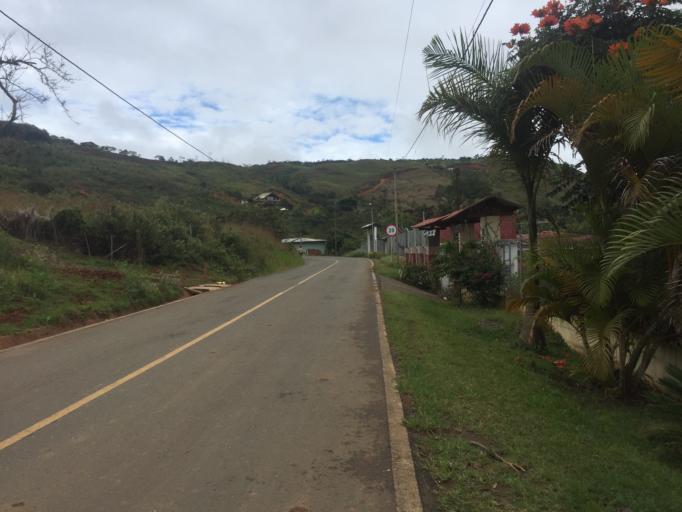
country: CO
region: Valle del Cauca
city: Dagua
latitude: 3.6876
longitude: -76.5927
